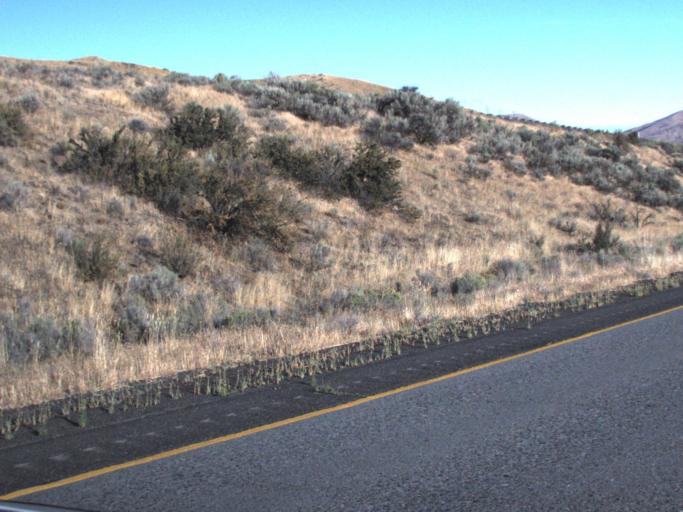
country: US
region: Washington
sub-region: Yakima County
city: Terrace Heights
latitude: 46.7354
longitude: -120.3849
